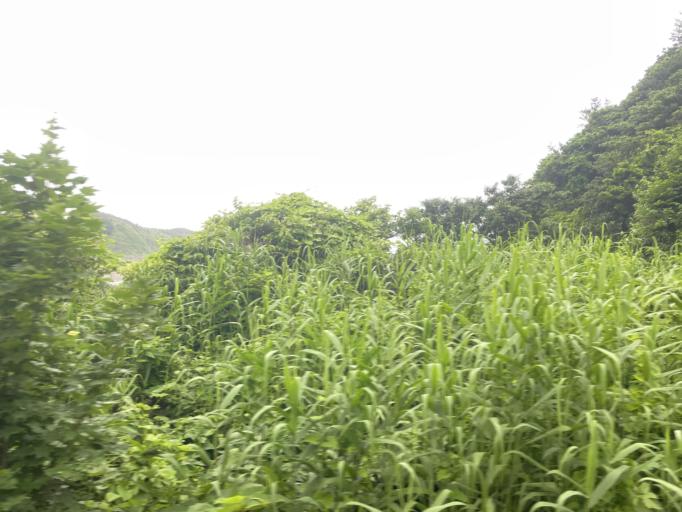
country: JP
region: Aomori
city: Shimokizukuri
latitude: 40.6879
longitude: 139.9684
